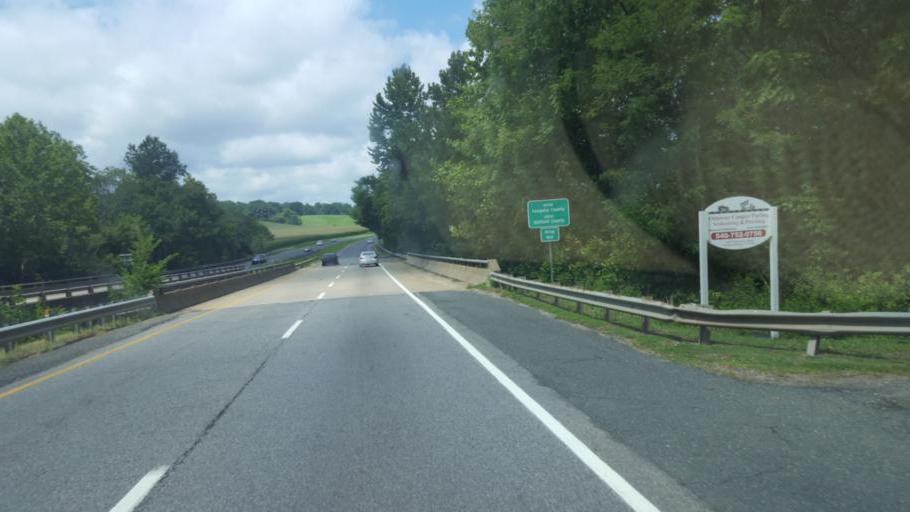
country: US
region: Virginia
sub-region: Stafford County
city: Falmouth
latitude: 38.4301
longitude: -77.6284
